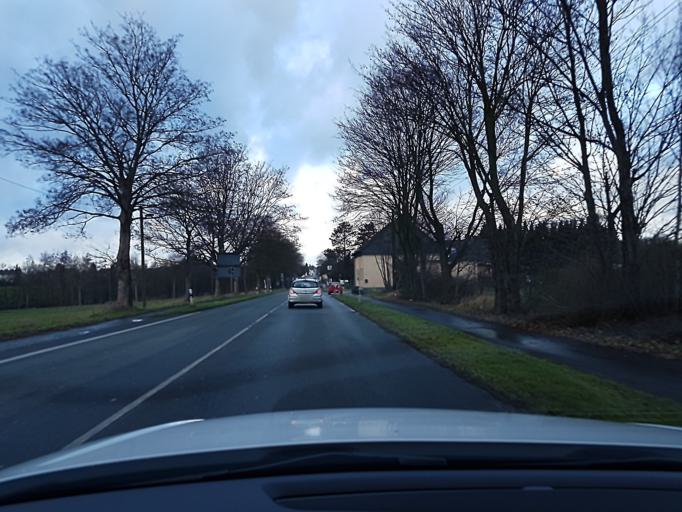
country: DE
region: North Rhine-Westphalia
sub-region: Regierungsbezirk Dusseldorf
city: Ratingen
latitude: 51.3616
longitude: 6.8632
